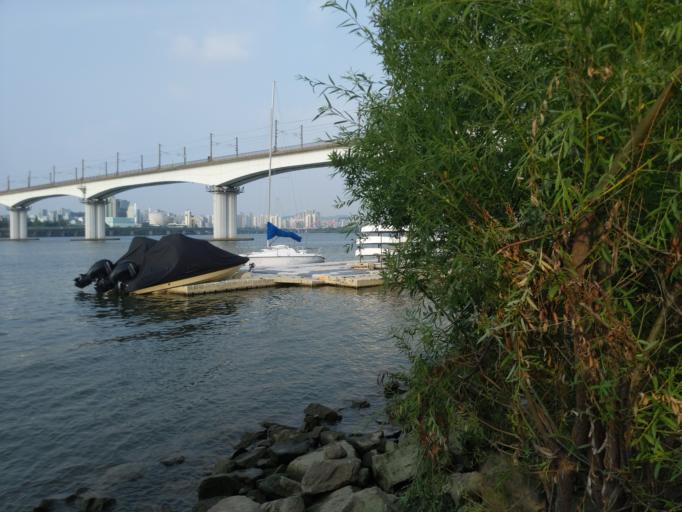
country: KR
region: Gyeonggi-do
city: Kwangmyong
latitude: 37.5383
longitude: 126.9042
